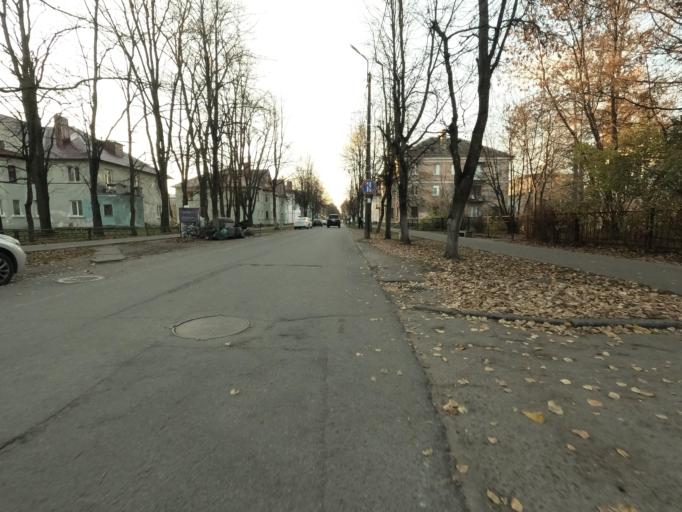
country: RU
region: Leningrad
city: Kirovsk
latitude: 59.8729
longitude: 30.9929
